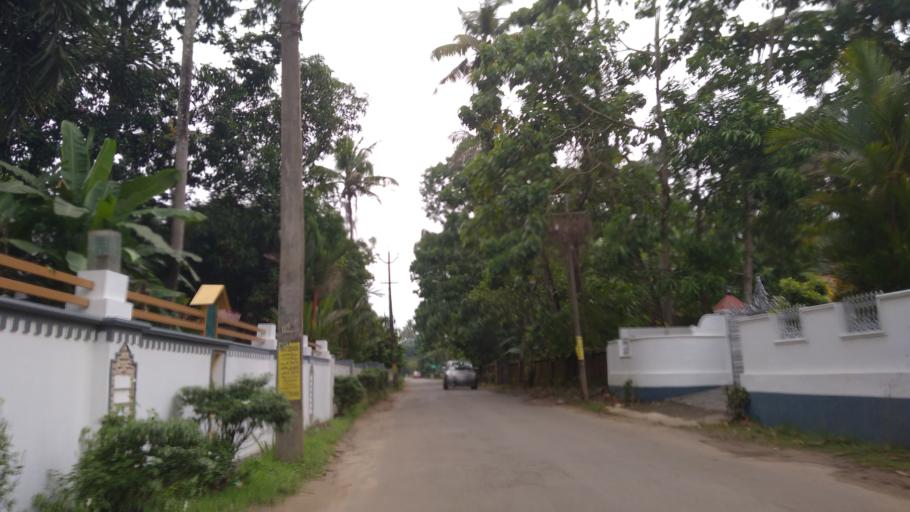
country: IN
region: Kerala
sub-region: Ernakulam
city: Kotamangalam
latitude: 10.1212
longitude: 76.5645
